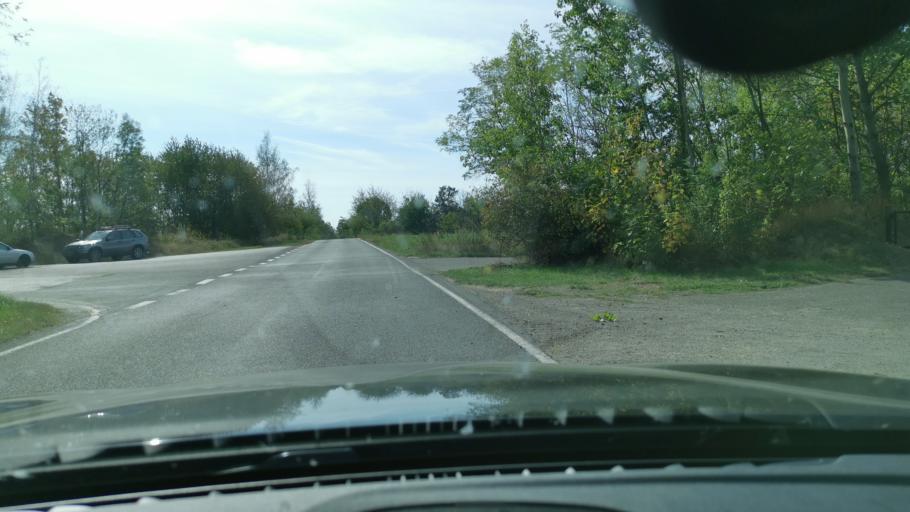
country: DE
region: Saxony
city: Hohburg
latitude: 51.4375
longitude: 12.7553
